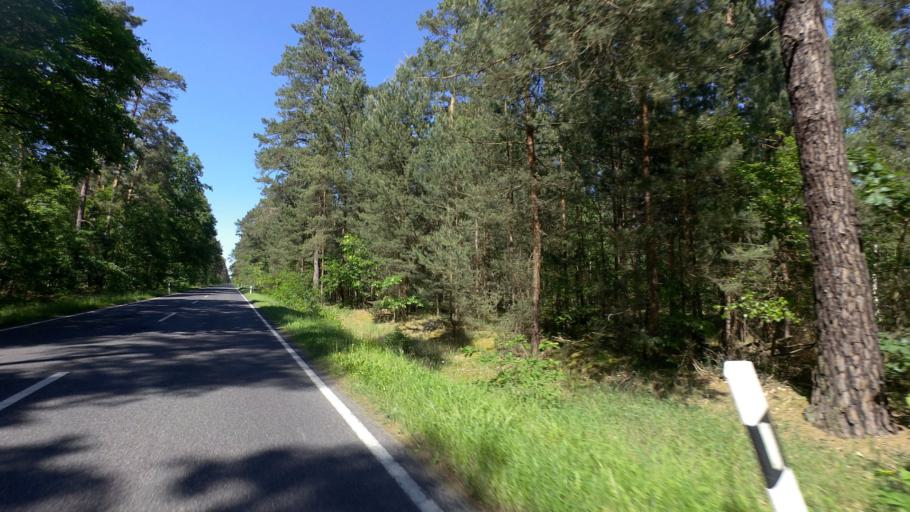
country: DE
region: Brandenburg
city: Gross Koris
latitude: 52.1991
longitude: 13.6944
